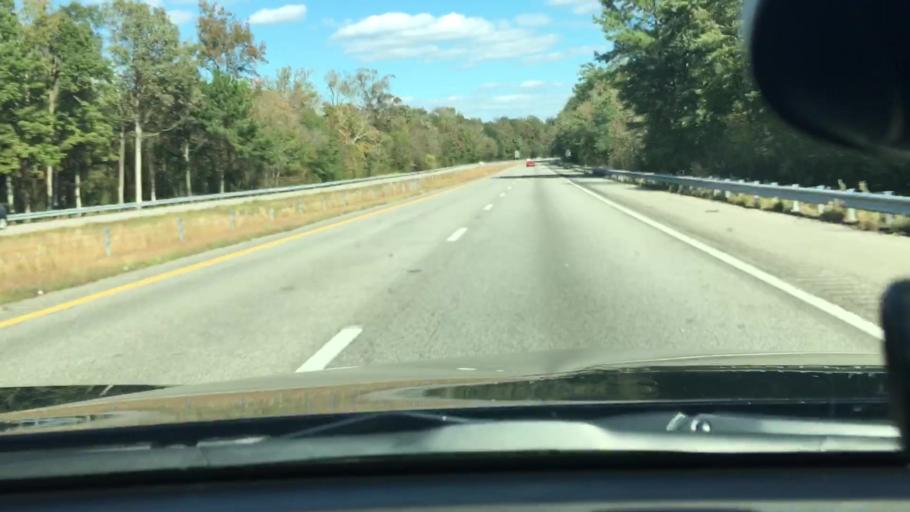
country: US
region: North Carolina
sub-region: Wilson County
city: Wilson
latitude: 35.6778
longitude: -77.8501
